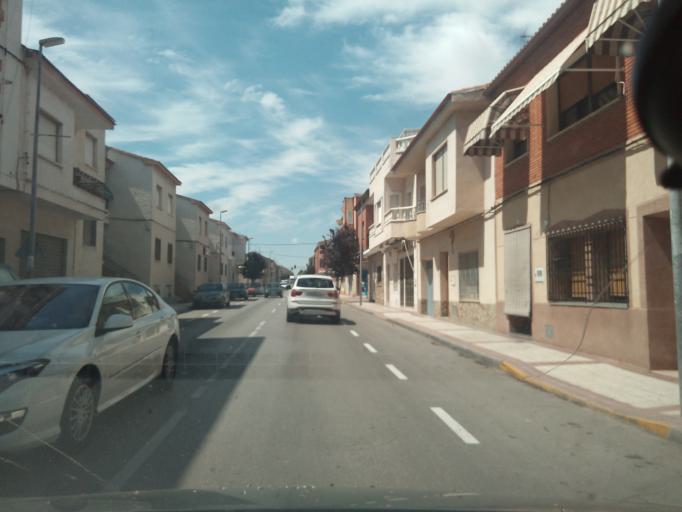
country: ES
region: Castille-La Mancha
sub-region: Province of Toledo
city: Villacanas
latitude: 39.6212
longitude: -3.3334
